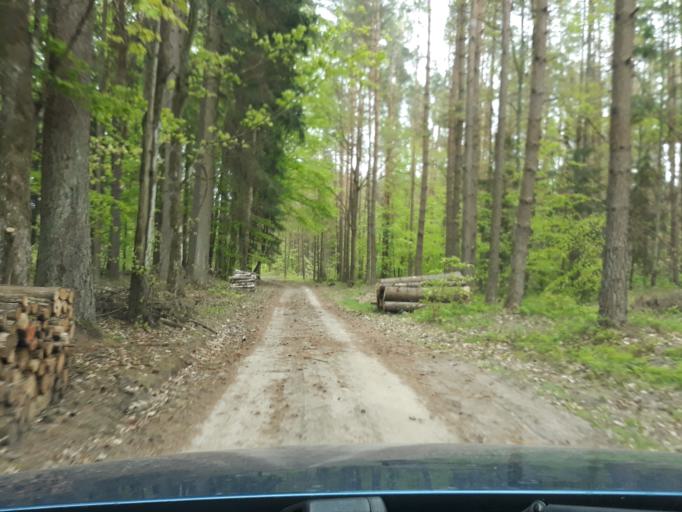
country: PL
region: Pomeranian Voivodeship
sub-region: Powiat czluchowski
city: Czluchow
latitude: 53.7561
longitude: 17.3495
